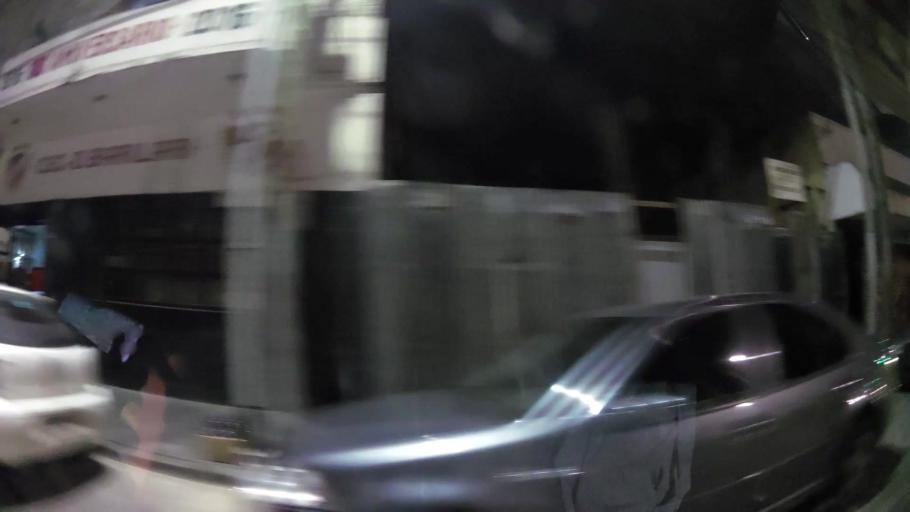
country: AR
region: Buenos Aires
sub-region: Partido de Avellaneda
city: Avellaneda
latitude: -34.6987
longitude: -58.3287
